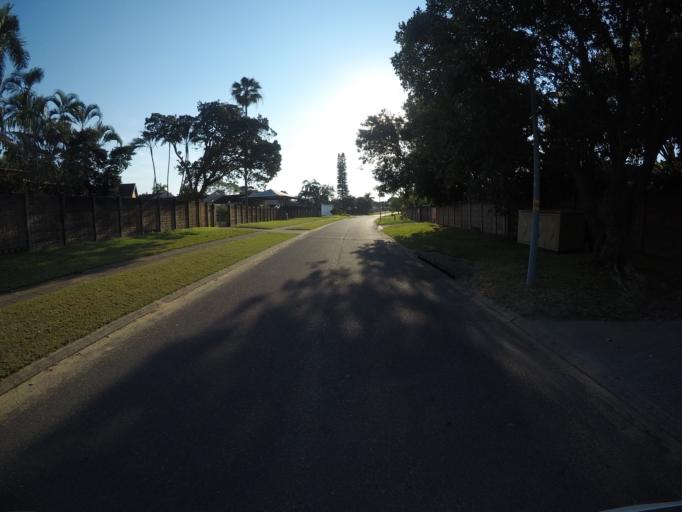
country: ZA
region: KwaZulu-Natal
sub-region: uThungulu District Municipality
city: Richards Bay
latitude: -28.7819
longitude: 32.1097
